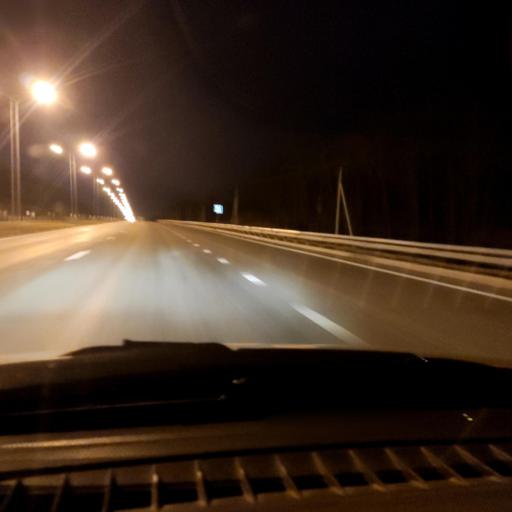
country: RU
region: Samara
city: Novosemeykino
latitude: 53.3762
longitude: 50.3112
